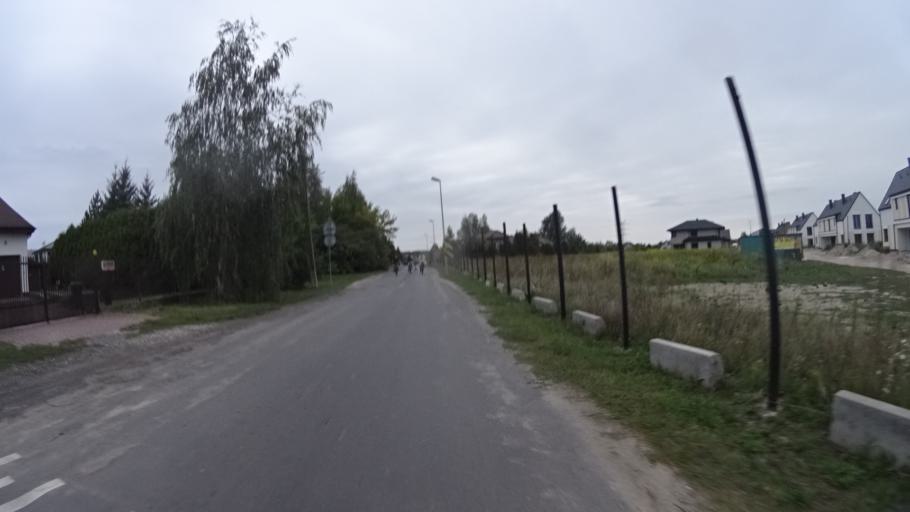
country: PL
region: Masovian Voivodeship
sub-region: Powiat warszawski zachodni
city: Stare Babice
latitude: 52.2558
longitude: 20.8214
